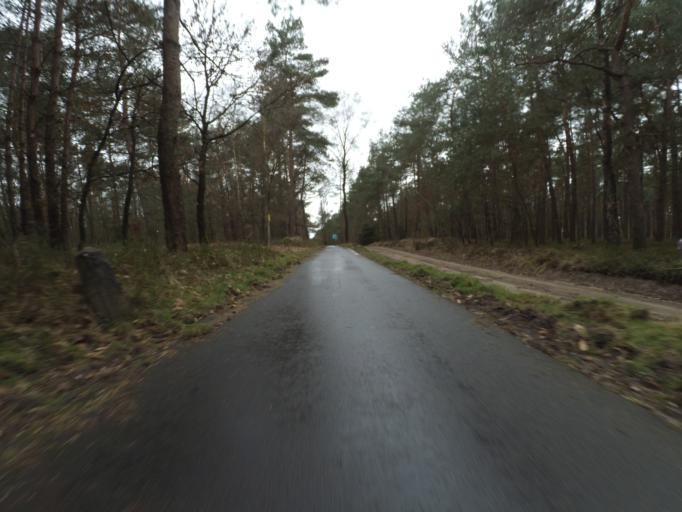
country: NL
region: Gelderland
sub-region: Gemeente Apeldoorn
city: Loenen
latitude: 52.0749
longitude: 6.0152
